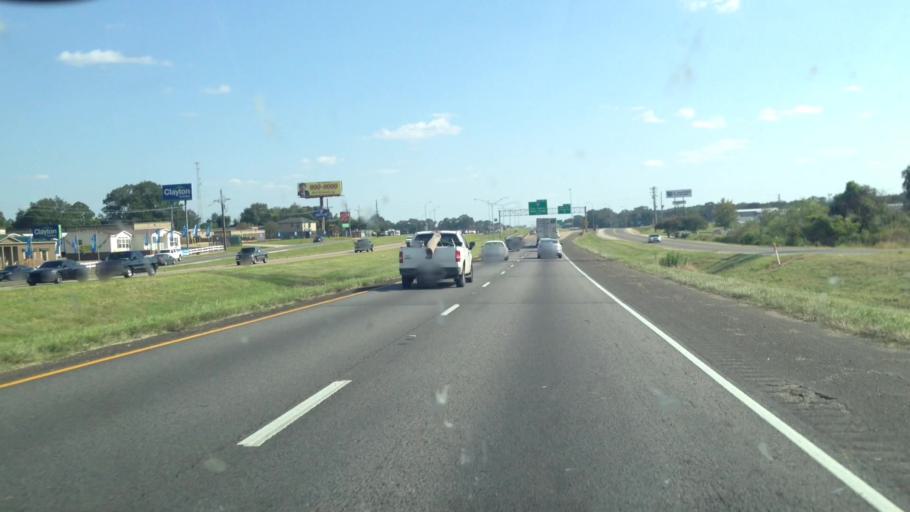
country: US
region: Louisiana
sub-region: Lafayette Parish
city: Carencro
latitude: 30.2807
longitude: -92.0207
